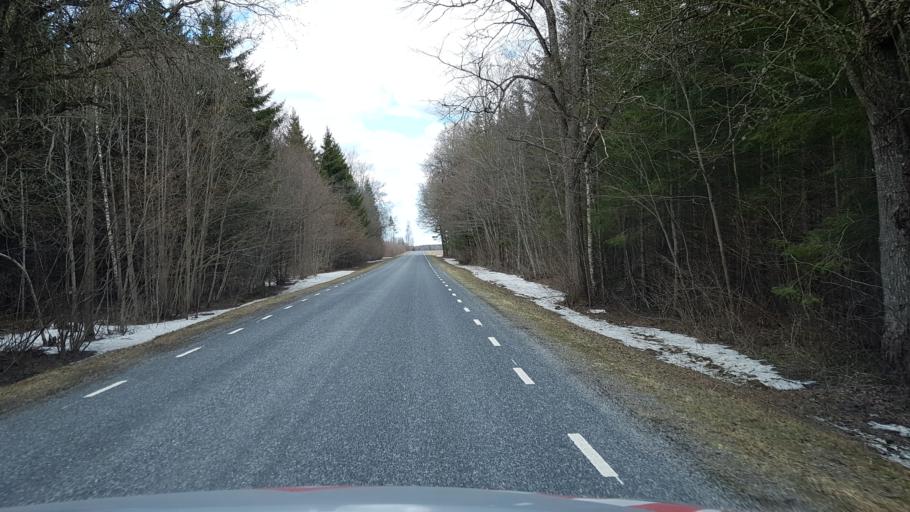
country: EE
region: Laeaene-Virumaa
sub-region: Tamsalu vald
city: Tamsalu
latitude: 59.1988
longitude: 26.1337
